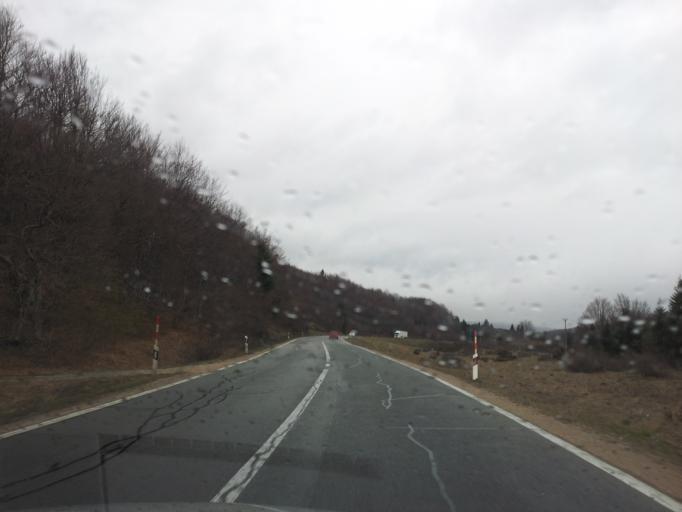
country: HR
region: Licko-Senjska
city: Jezerce
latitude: 44.8245
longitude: 15.6756
